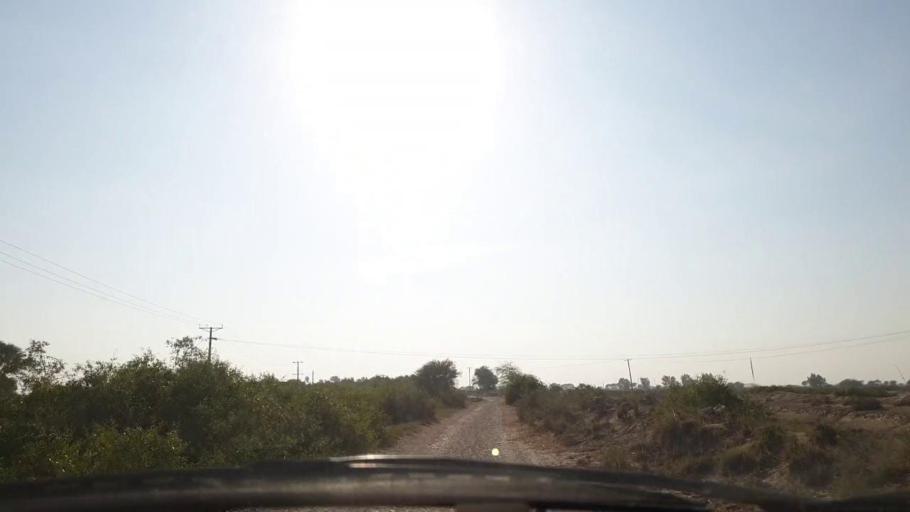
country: PK
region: Sindh
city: Bulri
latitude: 24.8155
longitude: 68.4016
